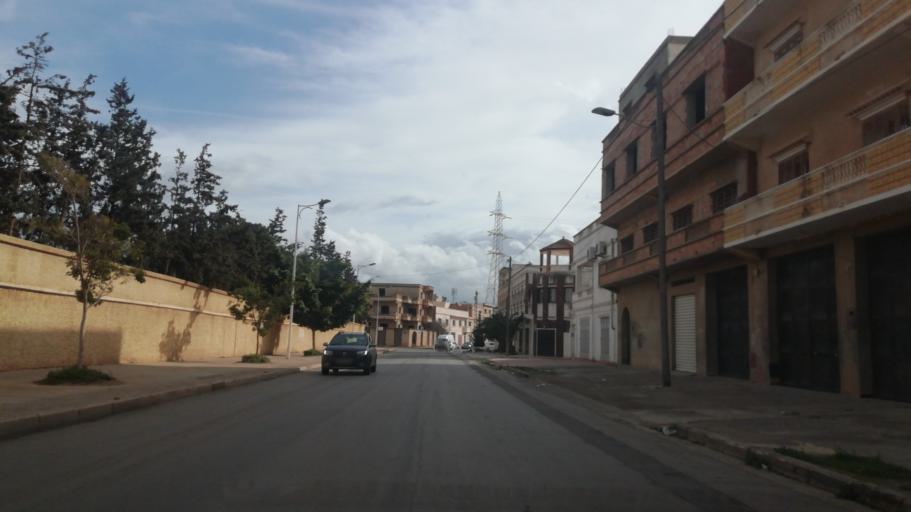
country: DZ
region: Oran
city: Es Senia
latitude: 35.6629
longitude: -0.6388
